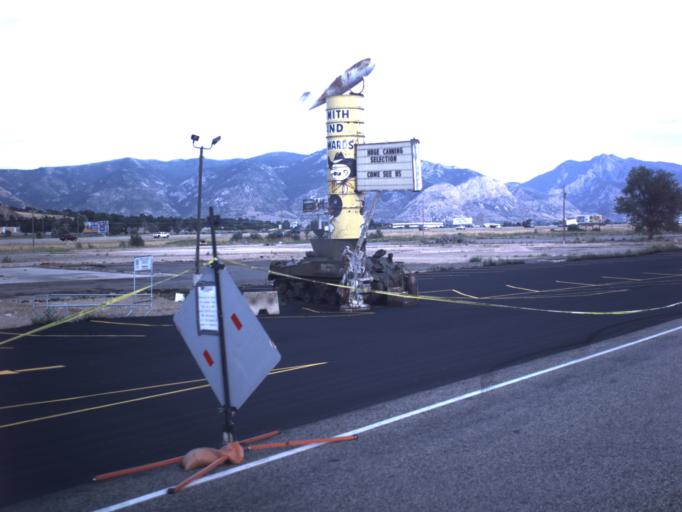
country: US
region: Utah
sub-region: Box Elder County
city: South Willard
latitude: 41.3338
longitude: -112.0362
